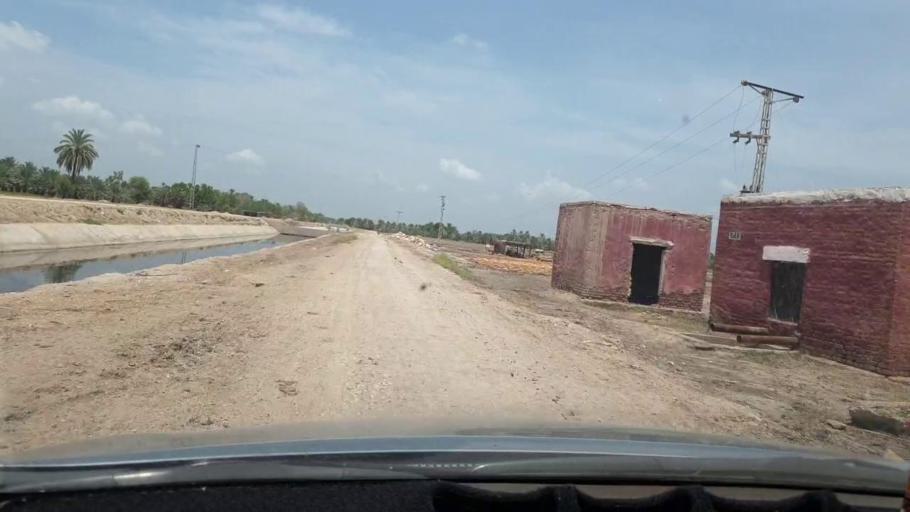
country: PK
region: Sindh
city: Khairpur
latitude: 27.4336
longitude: 68.7816
